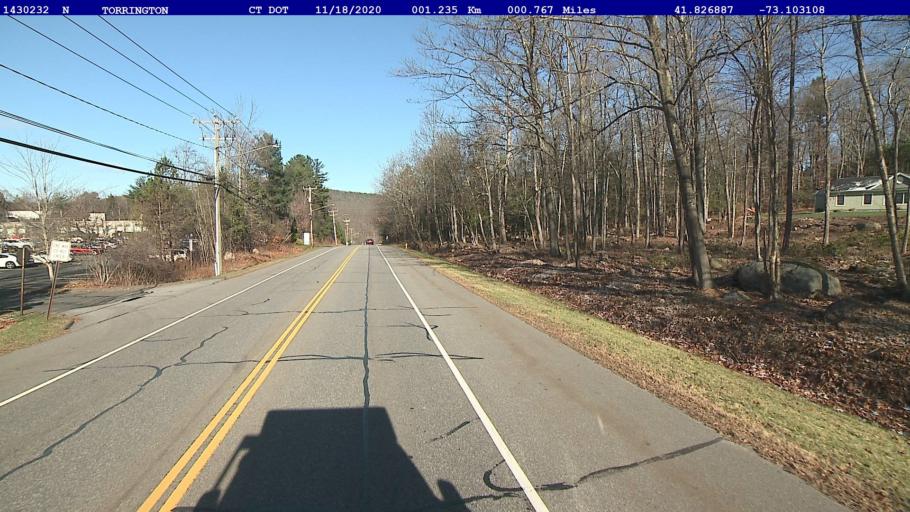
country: US
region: Connecticut
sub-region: Litchfield County
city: Torrington
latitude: 41.8269
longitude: -73.1031
